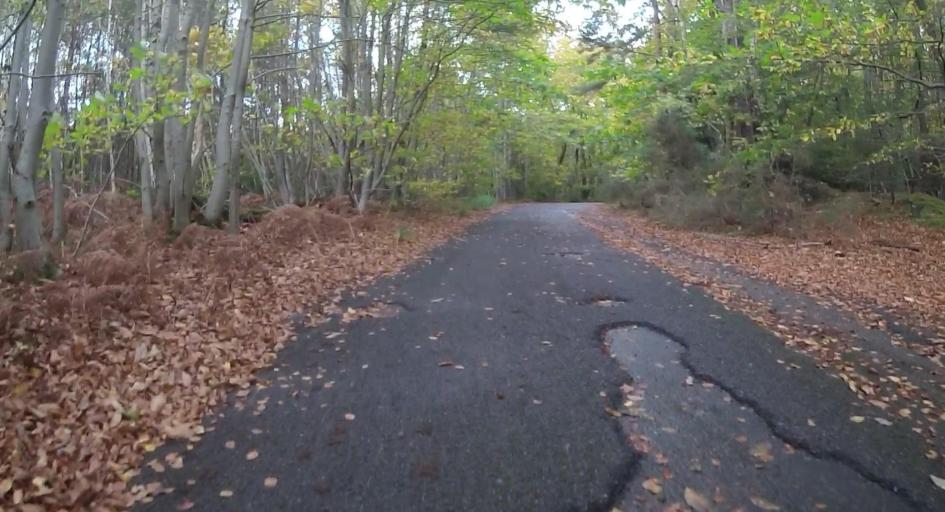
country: GB
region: England
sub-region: Surrey
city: Frimley
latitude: 51.3045
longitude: -0.7117
